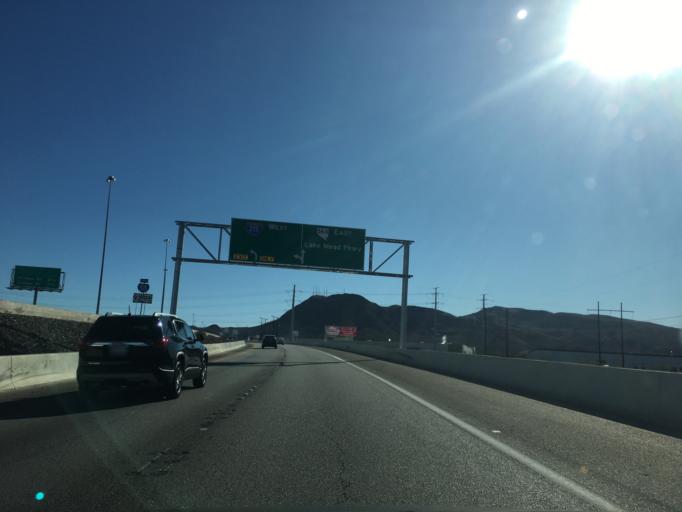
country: US
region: Nevada
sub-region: Clark County
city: Henderson
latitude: 36.0405
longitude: -115.0213
